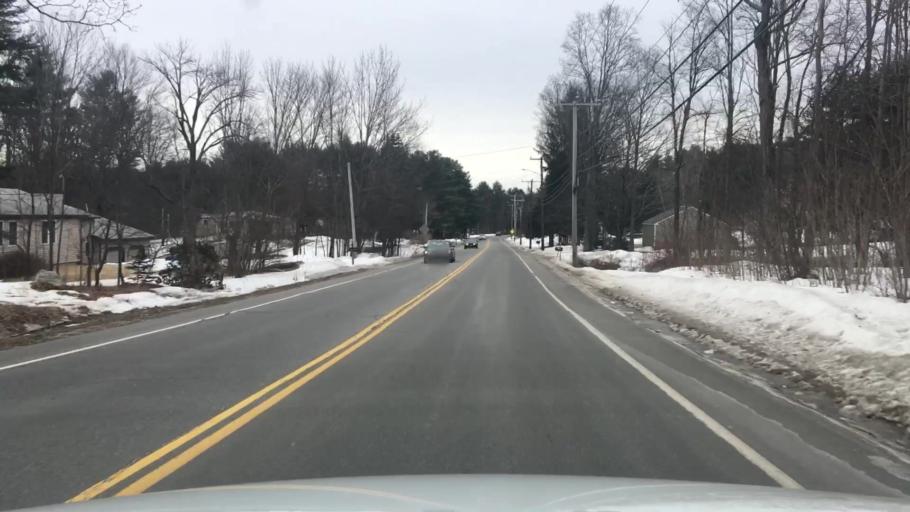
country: US
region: New Hampshire
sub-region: Strafford County
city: Rochester
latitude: 43.3723
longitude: -70.9848
